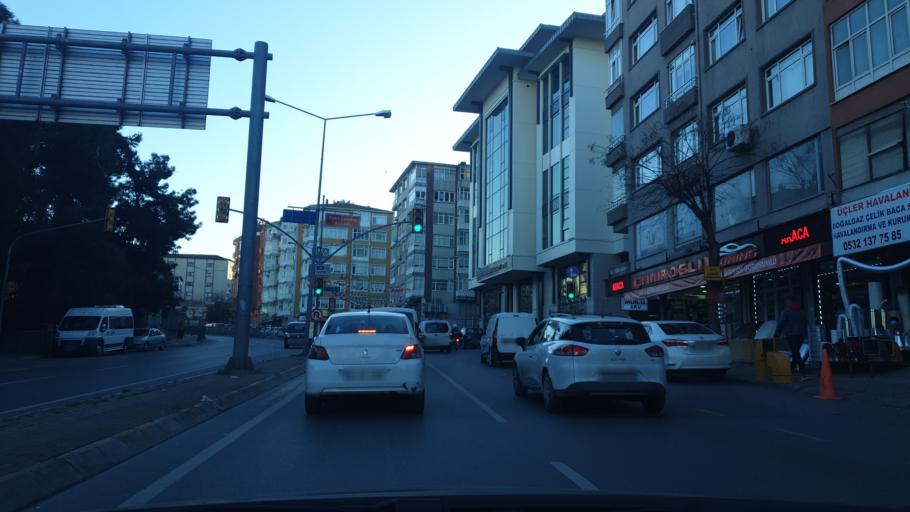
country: TR
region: Istanbul
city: merter keresteciler
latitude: 41.0105
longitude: 28.8759
